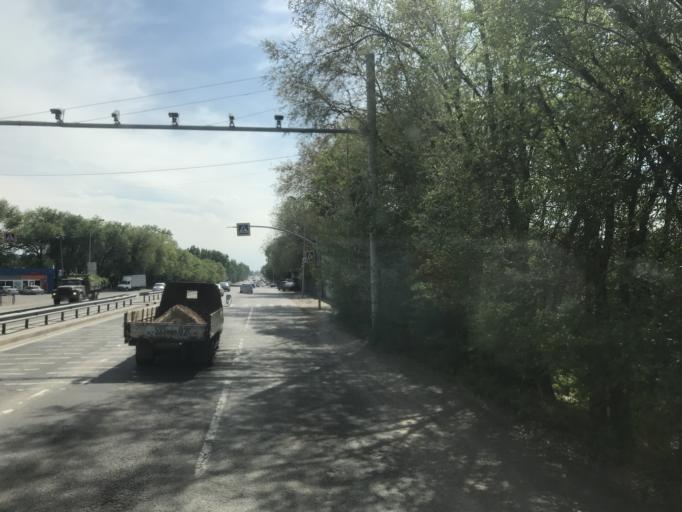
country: KZ
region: Almaty Oblysy
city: Pervomayskiy
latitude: 43.3356
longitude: 76.9154
